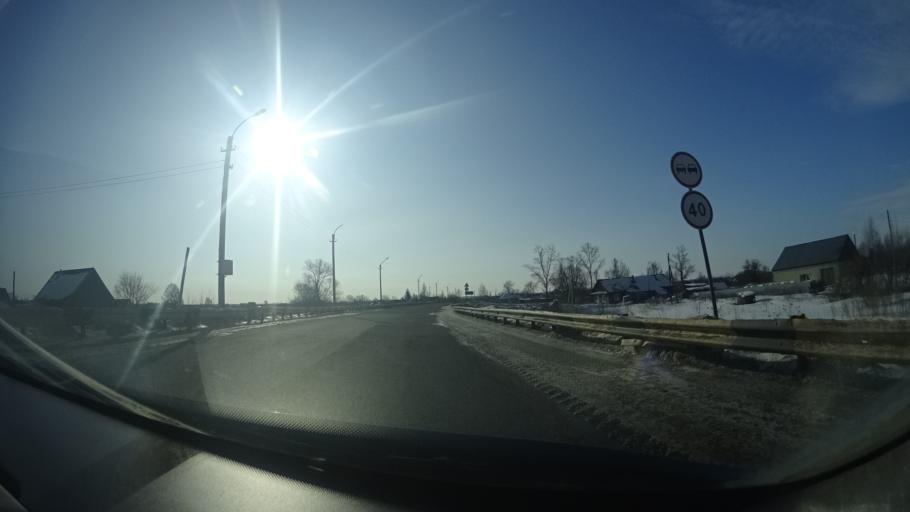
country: RU
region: Perm
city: Kuyeda
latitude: 56.4581
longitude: 55.5989
